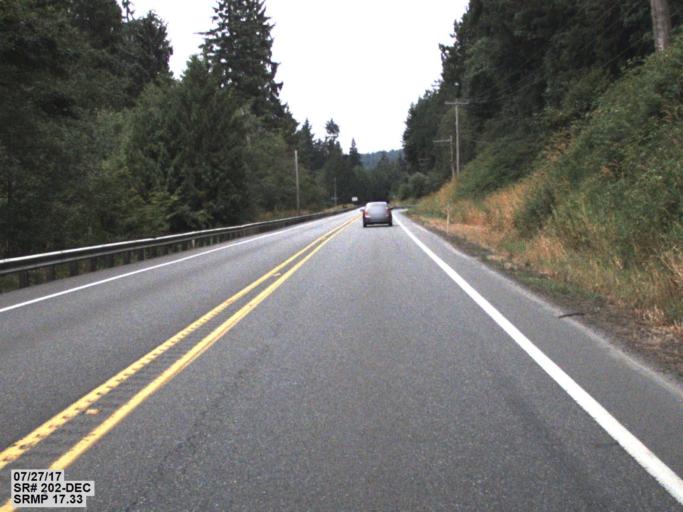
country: US
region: Washington
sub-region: King County
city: Ames Lake
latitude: 47.5998
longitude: -121.9617
